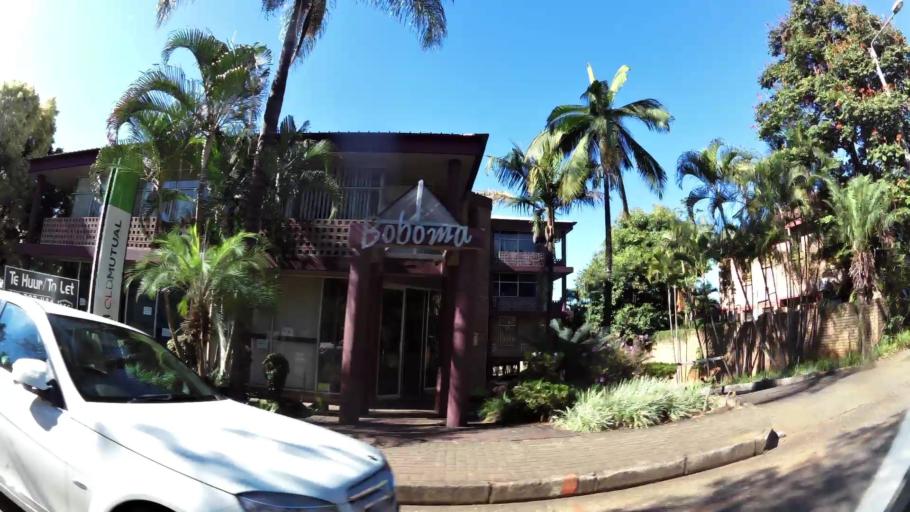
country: ZA
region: Limpopo
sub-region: Mopani District Municipality
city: Tzaneen
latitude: -23.8312
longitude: 30.1584
